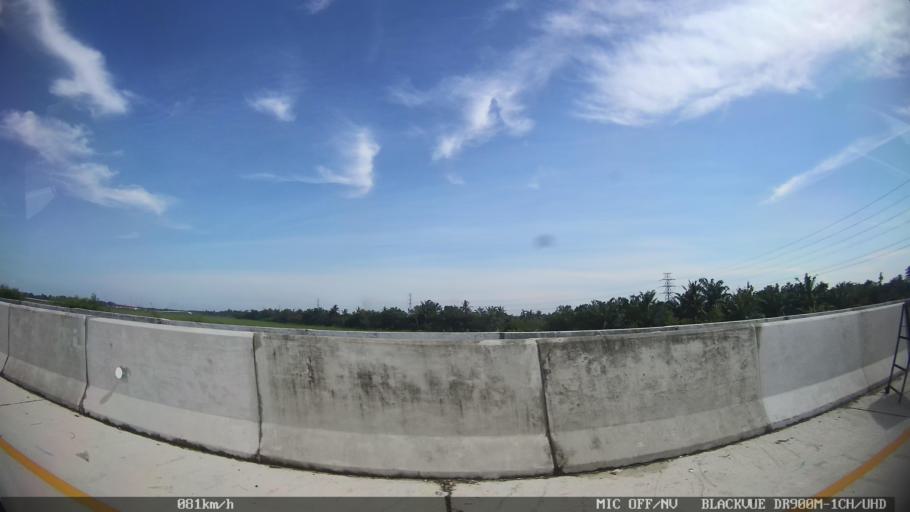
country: ID
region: North Sumatra
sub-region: Kabupaten Langkat
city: Stabat
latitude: 3.7134
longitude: 98.5022
